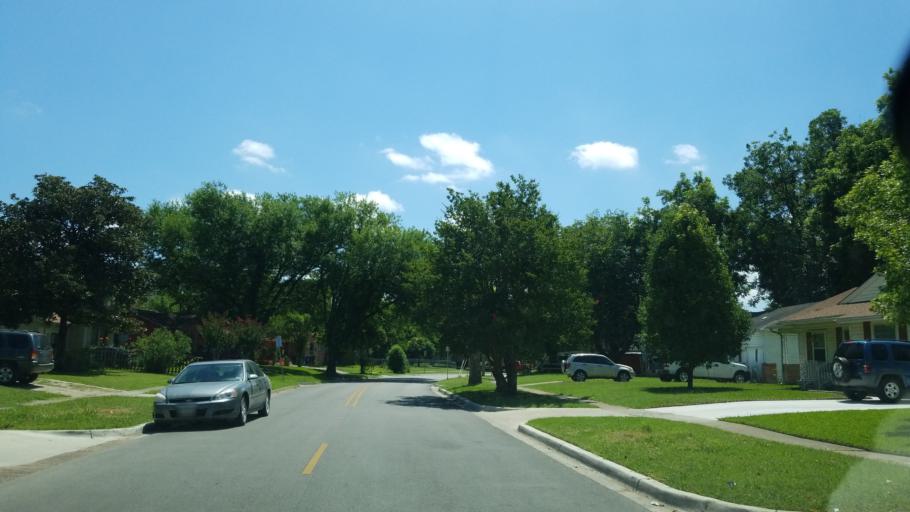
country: US
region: Texas
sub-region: Dallas County
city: Balch Springs
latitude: 32.7382
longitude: -96.6952
